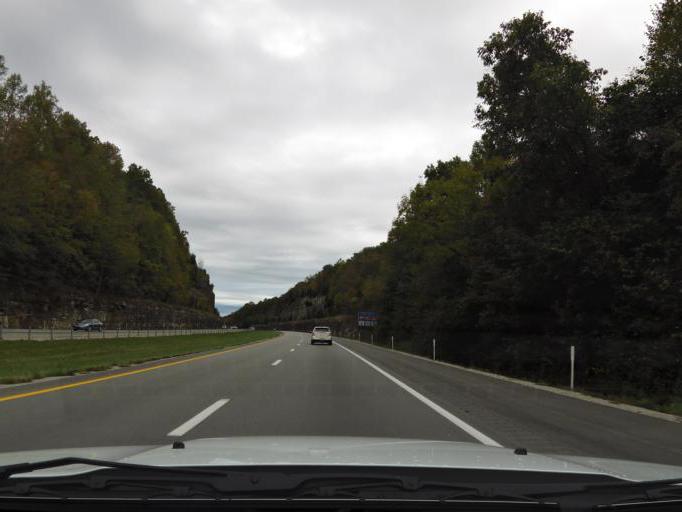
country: US
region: Kentucky
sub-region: Rockcastle County
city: Mount Vernon
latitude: 37.3640
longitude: -84.3099
